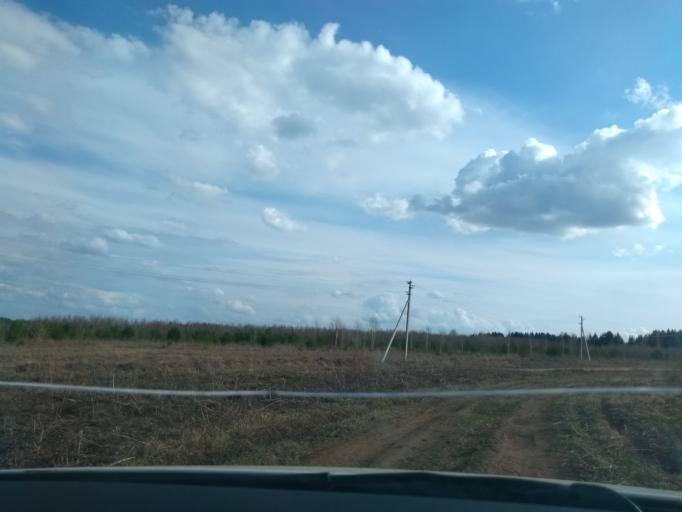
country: RU
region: Perm
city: Sylva
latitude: 57.8416
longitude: 56.7912
